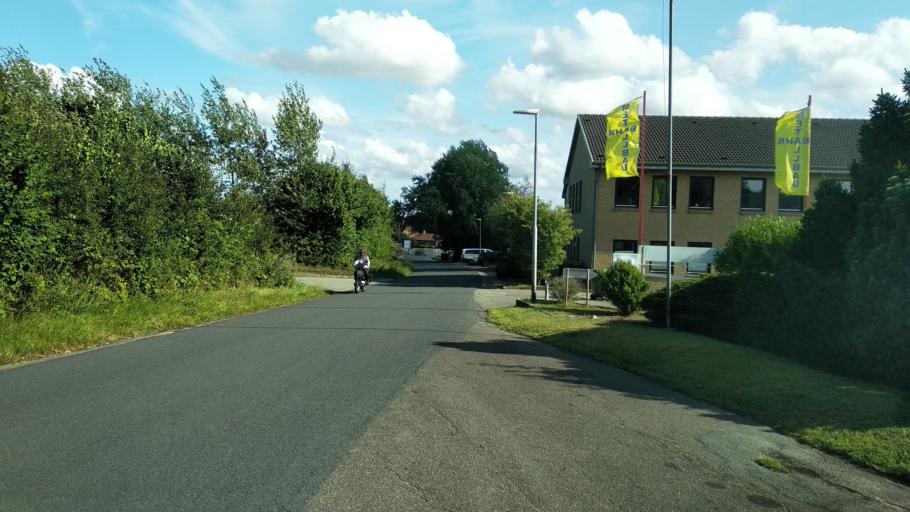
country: DE
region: Schleswig-Holstein
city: Schleswig
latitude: 54.5351
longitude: 9.5554
